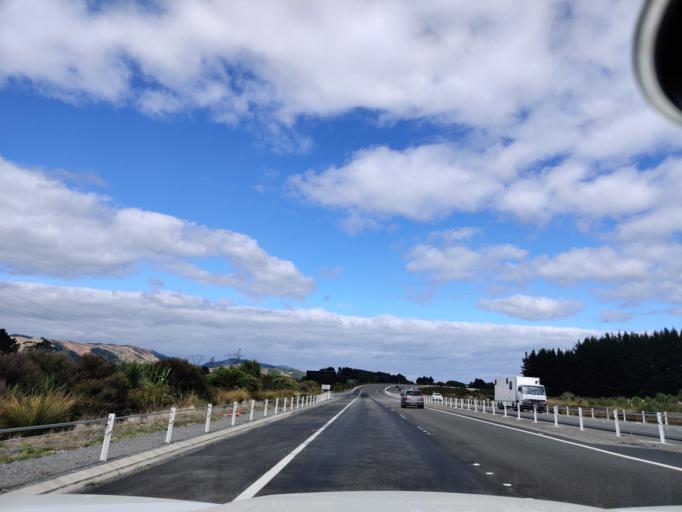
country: NZ
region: Wellington
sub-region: Kapiti Coast District
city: Paraparaumu
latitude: -40.8536
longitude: 175.0604
